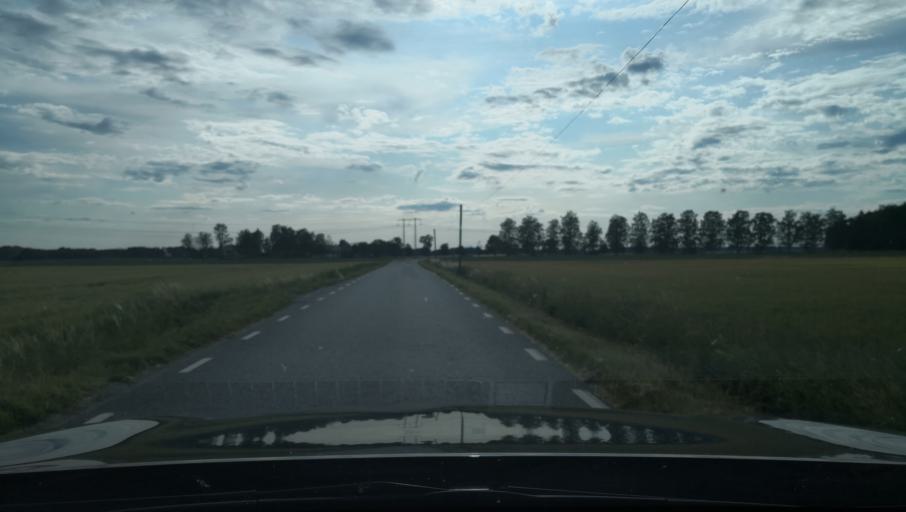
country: SE
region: Uppsala
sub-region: Enkopings Kommun
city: Orsundsbro
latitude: 59.6927
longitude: 17.3393
